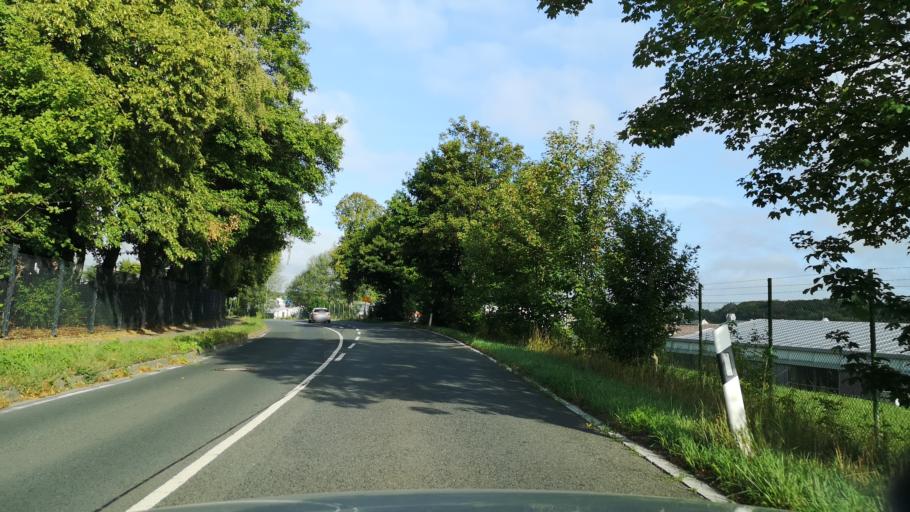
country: DE
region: North Rhine-Westphalia
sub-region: Regierungsbezirk Dusseldorf
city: Wuppertal
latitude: 51.3082
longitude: 7.1145
